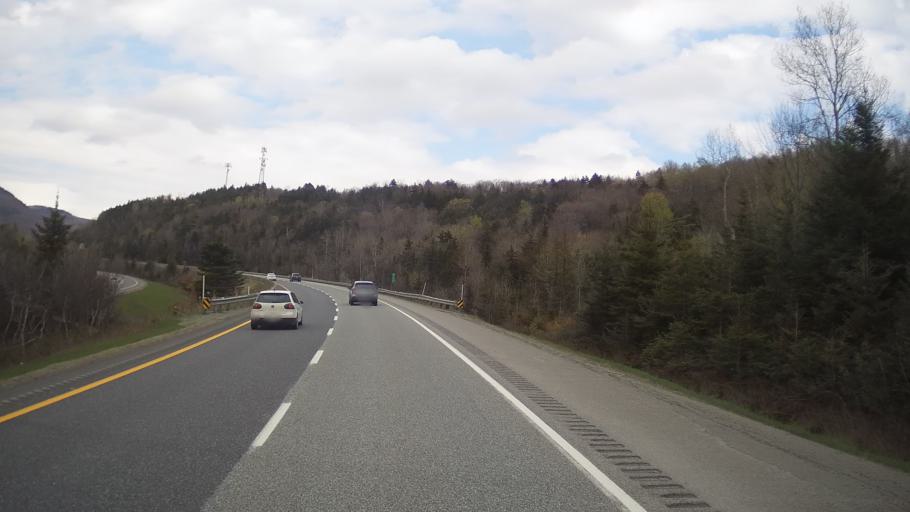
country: CA
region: Quebec
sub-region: Estrie
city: Magog
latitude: 45.2855
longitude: -72.2762
